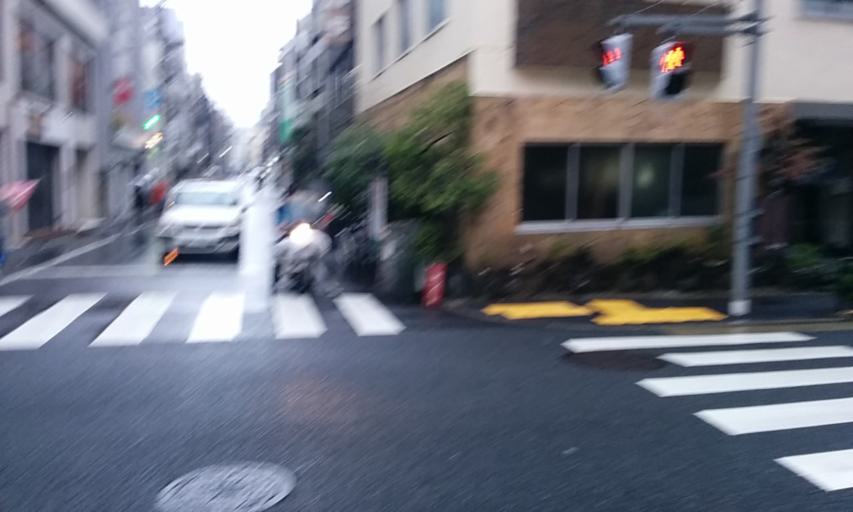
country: JP
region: Tokyo
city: Tokyo
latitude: 35.7056
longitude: 139.7632
